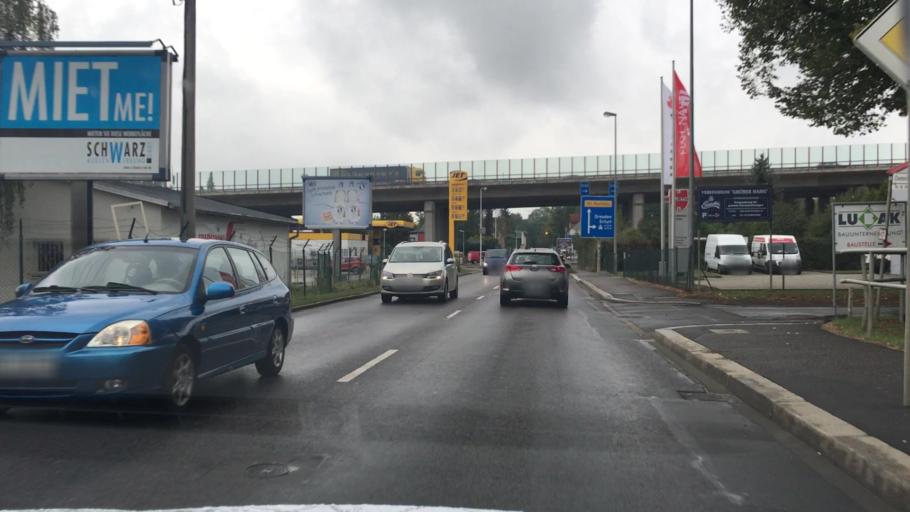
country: DE
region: Saxony
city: Wittgensdorf
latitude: 50.8726
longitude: 12.9086
